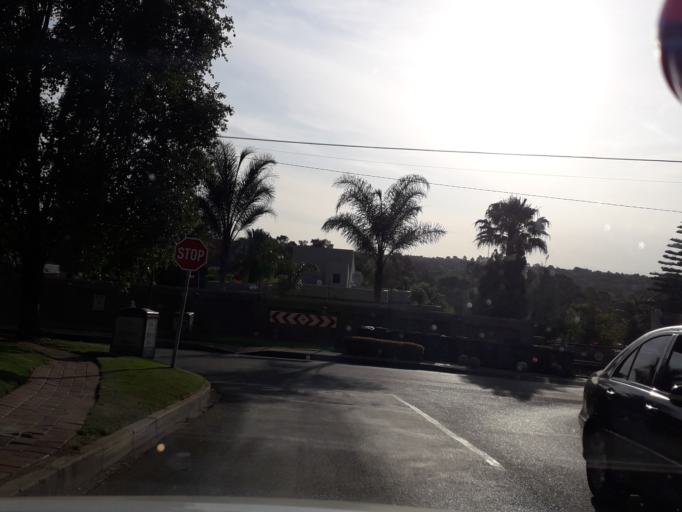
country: ZA
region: Gauteng
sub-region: City of Johannesburg Metropolitan Municipality
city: Diepsloot
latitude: -26.0455
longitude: 27.9899
